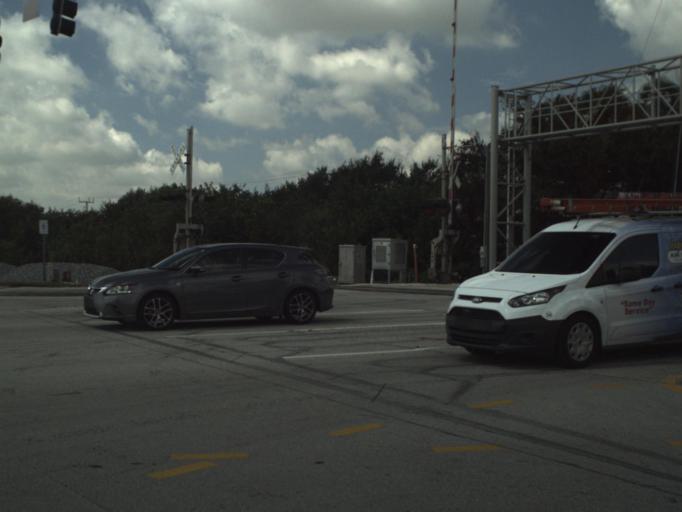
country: US
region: Florida
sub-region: Palm Beach County
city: North Palm Beach
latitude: 26.8307
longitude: -80.0918
